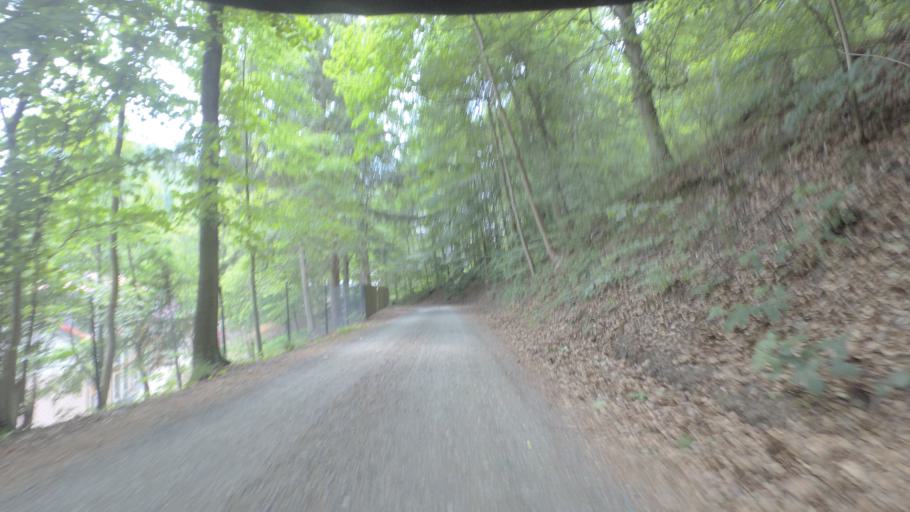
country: DE
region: Lower Saxony
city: Bad Harzburg
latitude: 51.8732
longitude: 10.5532
